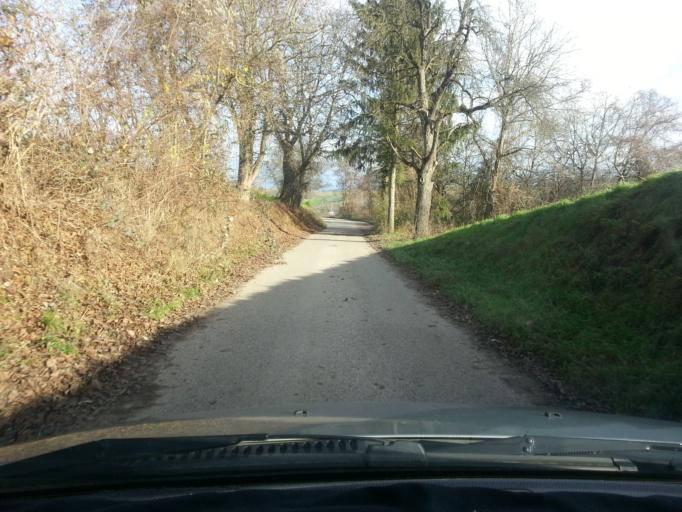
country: DE
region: Baden-Wuerttemberg
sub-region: Karlsruhe Region
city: Ostringen
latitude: 49.2041
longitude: 8.7310
